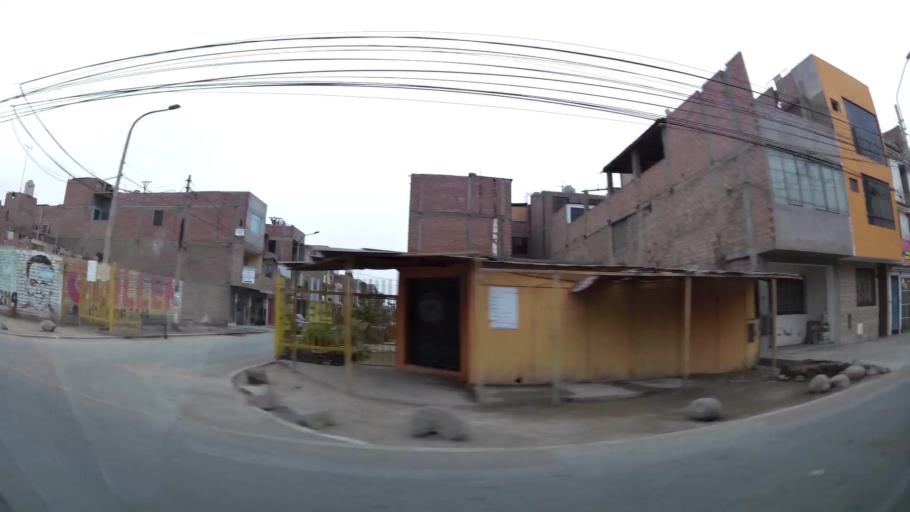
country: PE
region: Lima
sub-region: Lima
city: Urb. Santo Domingo
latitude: -11.9225
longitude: -77.0543
